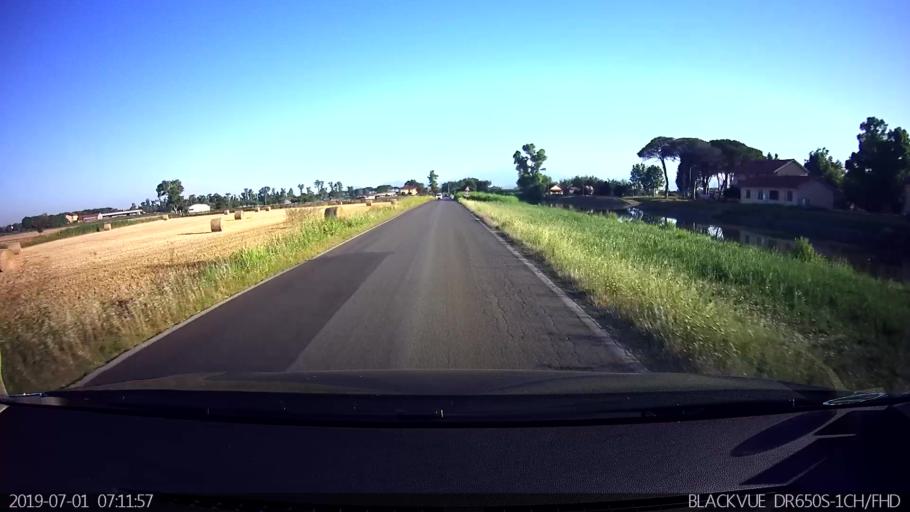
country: IT
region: Latium
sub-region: Provincia di Latina
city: Borgo Hermada
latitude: 41.3255
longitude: 13.1755
